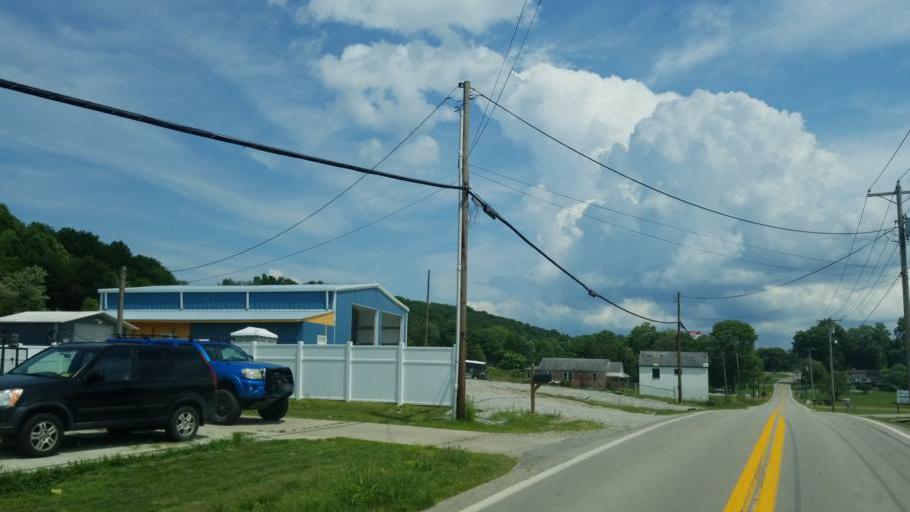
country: US
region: West Virginia
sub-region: Kanawha County
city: Nitro
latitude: 38.4535
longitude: -81.8654
